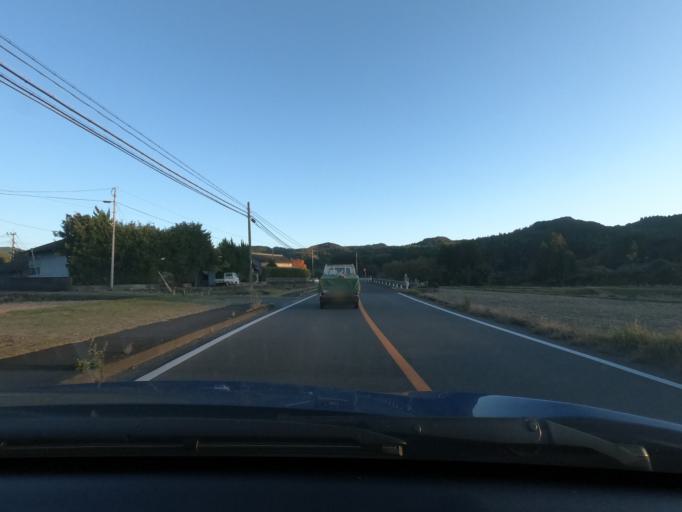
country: JP
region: Kagoshima
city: Satsumasendai
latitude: 31.7929
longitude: 130.4509
